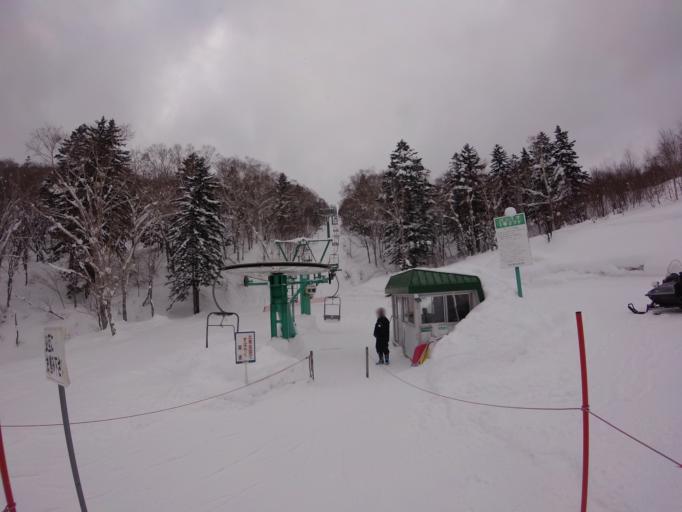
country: JP
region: Hokkaido
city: Sapporo
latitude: 43.0698
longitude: 141.2080
